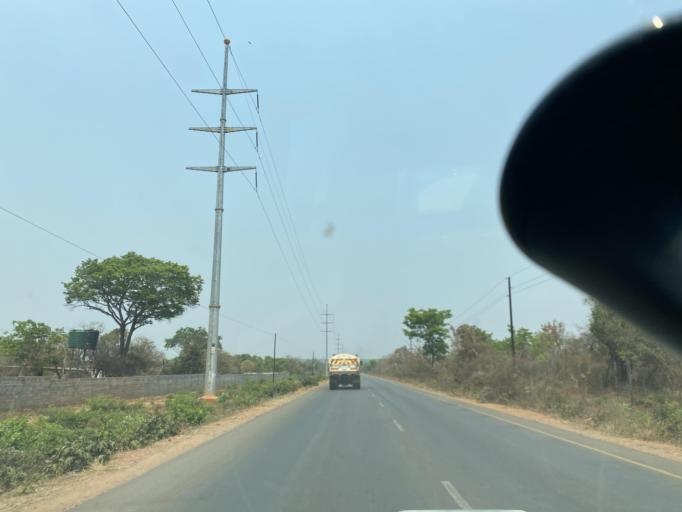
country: ZM
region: Lusaka
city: Lusaka
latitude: -15.5167
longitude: 28.4545
